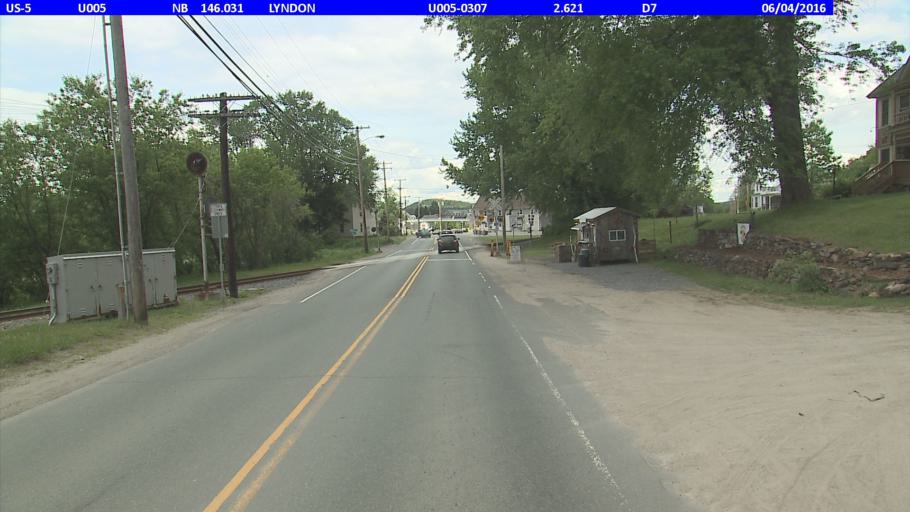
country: US
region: Vermont
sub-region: Caledonia County
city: Lyndonville
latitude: 44.5310
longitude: -72.0021
